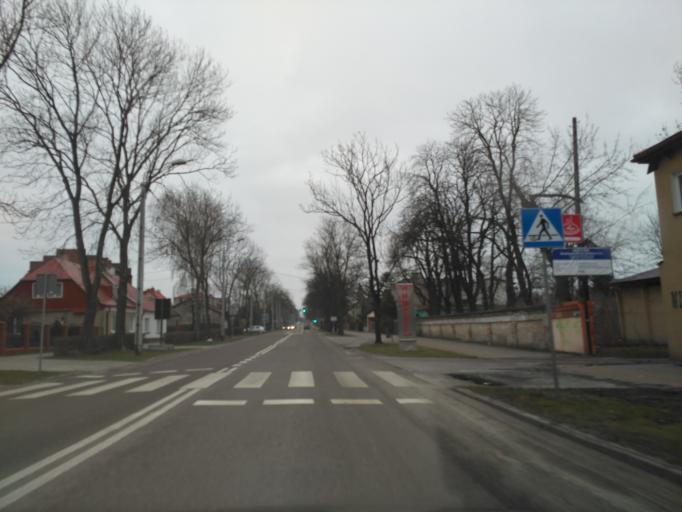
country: PL
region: Lublin Voivodeship
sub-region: Chelm
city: Chelm
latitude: 51.1279
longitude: 23.4874
